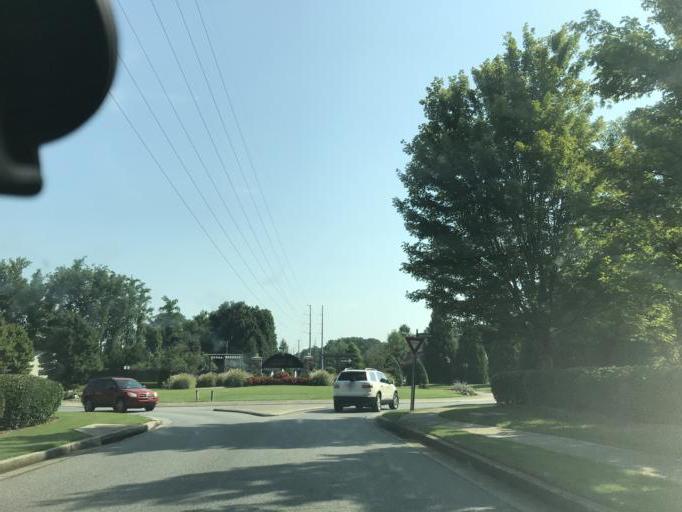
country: US
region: Georgia
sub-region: Forsyth County
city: Cumming
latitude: 34.2364
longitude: -84.1026
